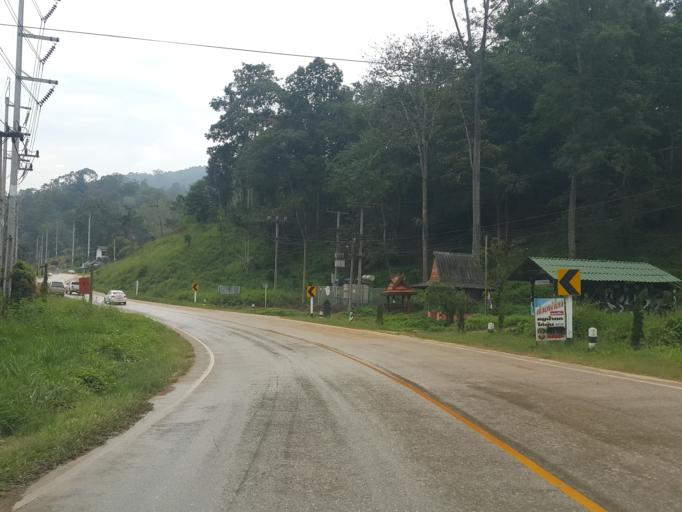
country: TH
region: Chiang Mai
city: Mae Taeng
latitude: 19.1655
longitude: 98.6907
